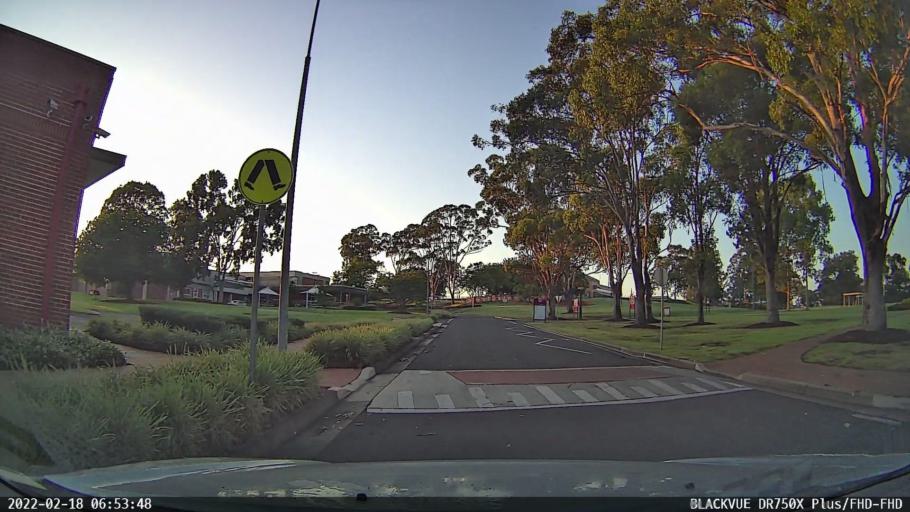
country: AU
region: New South Wales
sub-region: Penrith Municipality
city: Kingswood Park
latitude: -33.7652
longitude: 150.7280
